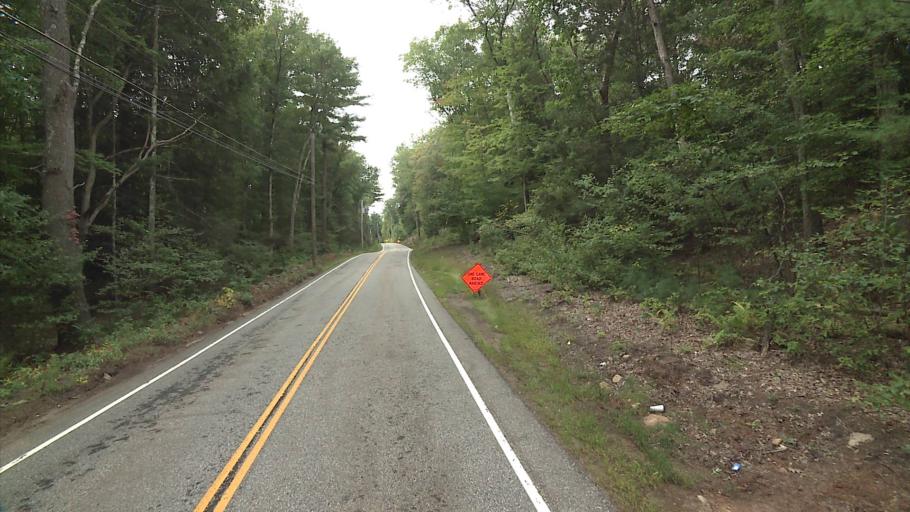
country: US
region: Connecticut
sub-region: Tolland County
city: Stafford Springs
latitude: 41.9058
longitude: -72.2651
